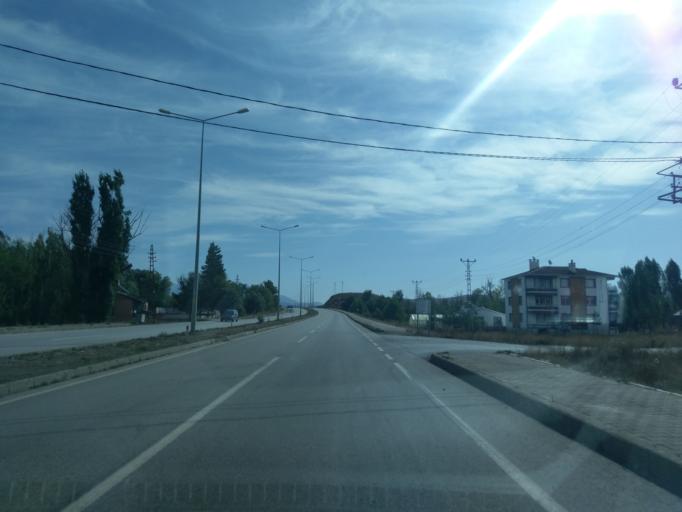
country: TR
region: Sivas
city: Imranli
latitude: 39.8707
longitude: 38.1216
